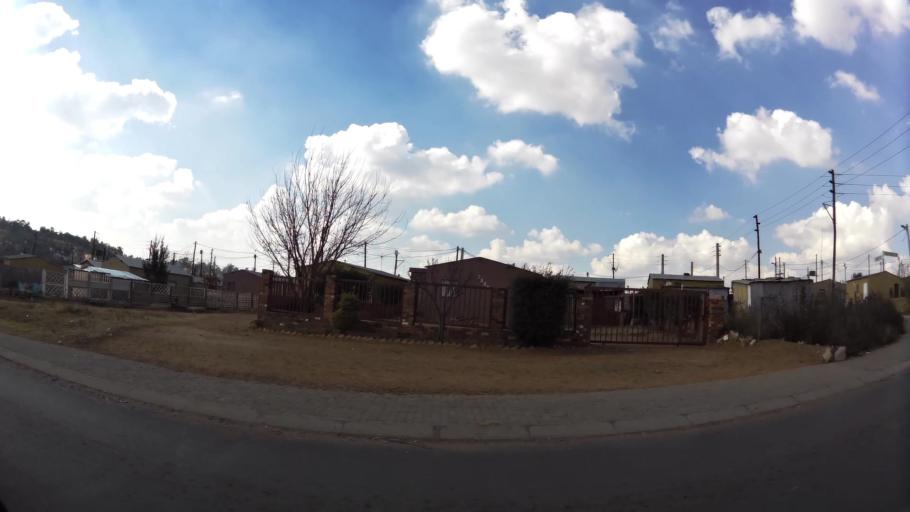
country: ZA
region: Gauteng
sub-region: City of Johannesburg Metropolitan Municipality
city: Roodepoort
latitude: -26.1825
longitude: 27.8542
